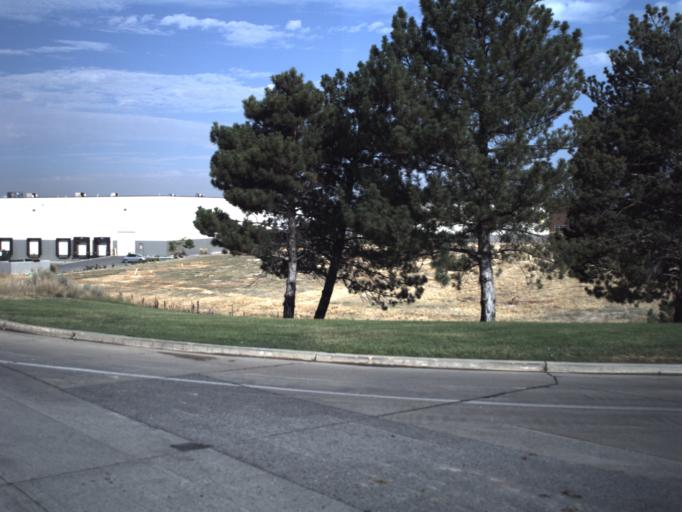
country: US
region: Utah
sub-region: Salt Lake County
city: West Valley City
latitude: 40.7721
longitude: -112.0252
